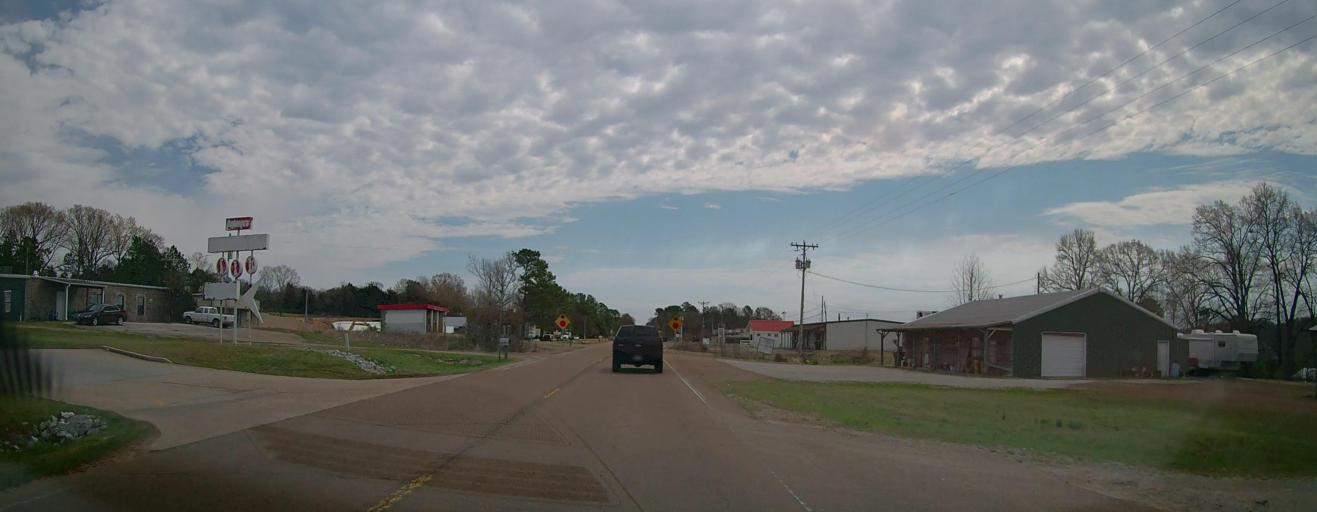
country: US
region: Mississippi
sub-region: Marshall County
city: Byhalia
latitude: 34.8295
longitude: -89.5689
